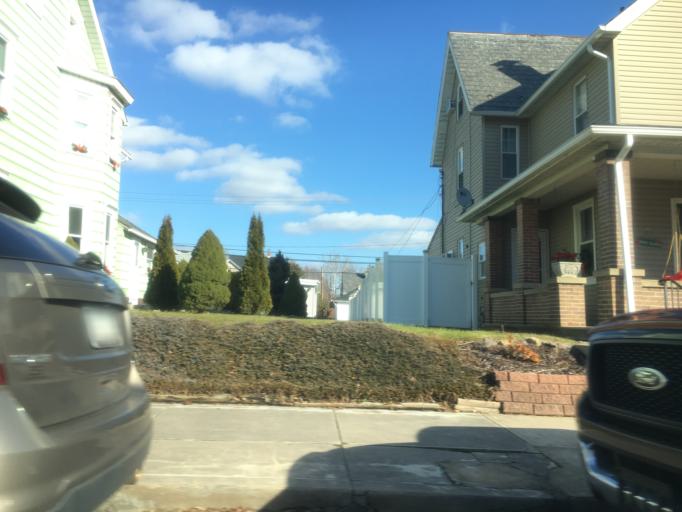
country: US
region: Pennsylvania
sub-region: Northampton County
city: Northampton
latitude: 40.6814
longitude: -75.4920
